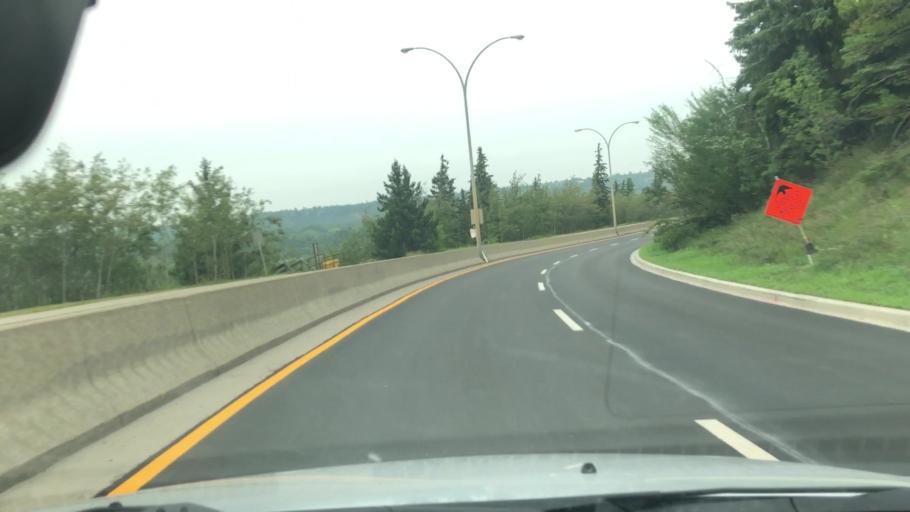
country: CA
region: Alberta
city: Edmonton
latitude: 53.5240
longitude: -113.5420
